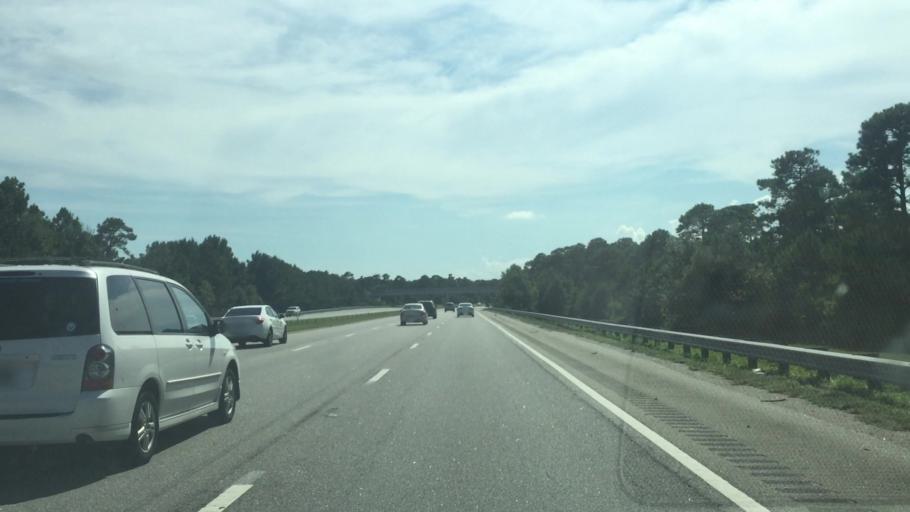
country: US
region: South Carolina
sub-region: Horry County
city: North Myrtle Beach
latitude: 33.8290
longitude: -78.7211
